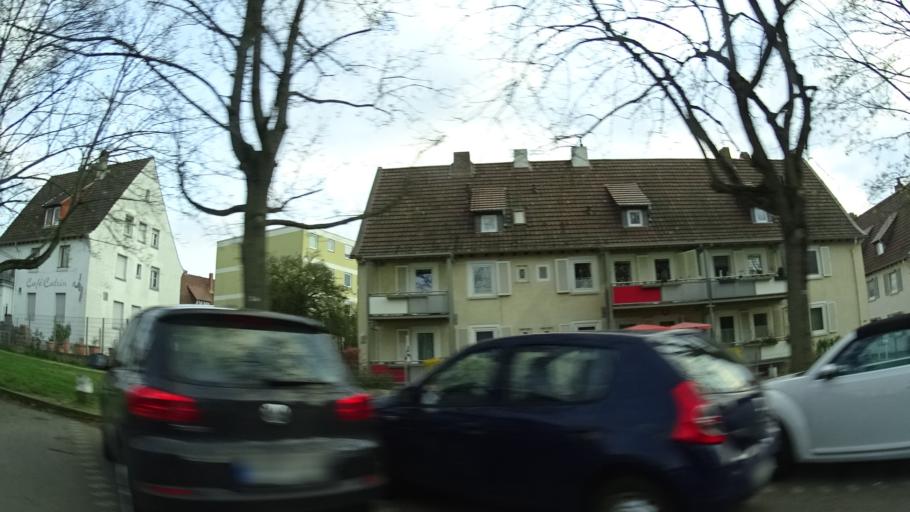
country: DE
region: Rheinland-Pfalz
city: Bad Kreuznach
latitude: 49.8346
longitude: 7.8722
